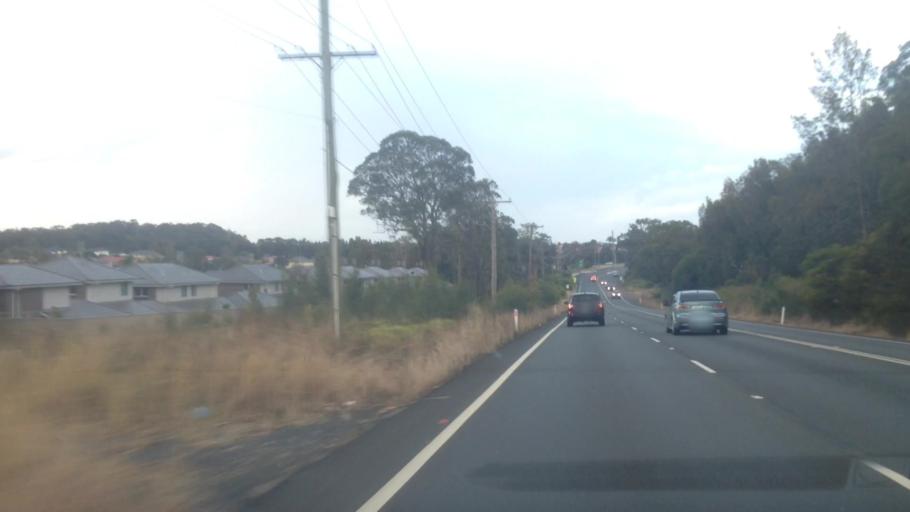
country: AU
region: New South Wales
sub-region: Wyong Shire
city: Kanwal
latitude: -33.2565
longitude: 151.4865
